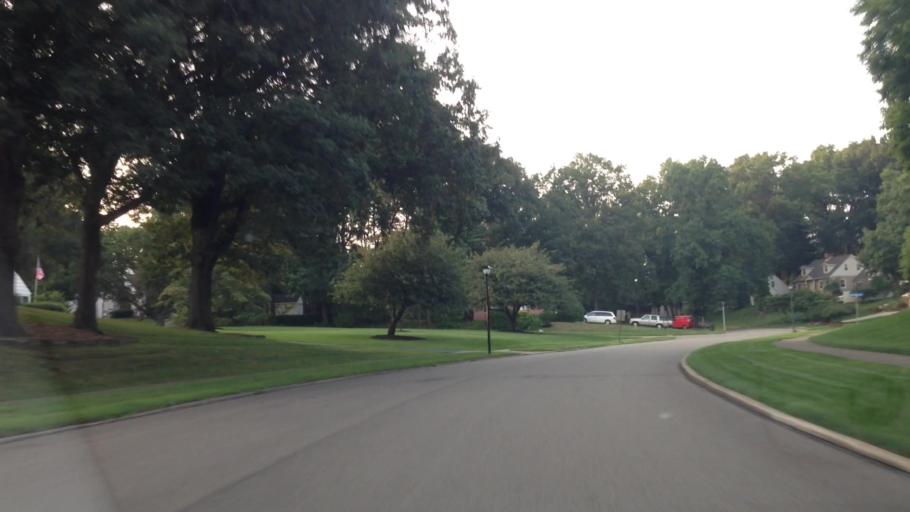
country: US
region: Ohio
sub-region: Stark County
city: Massillon
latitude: 40.8168
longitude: -81.5110
